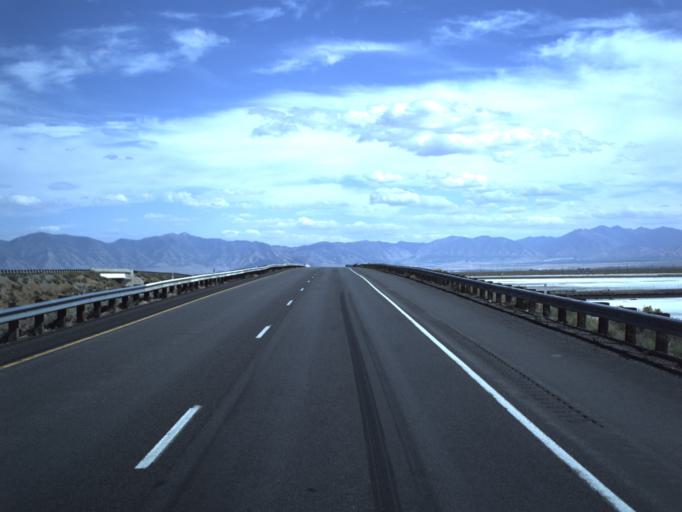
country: US
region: Utah
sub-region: Tooele County
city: Grantsville
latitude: 40.7104
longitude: -112.5325
